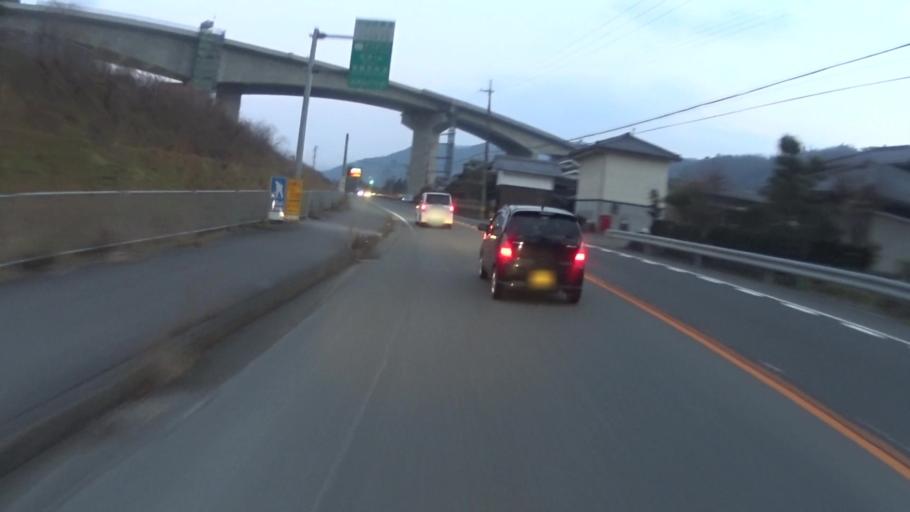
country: JP
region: Kyoto
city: Ayabe
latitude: 35.2773
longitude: 135.3362
